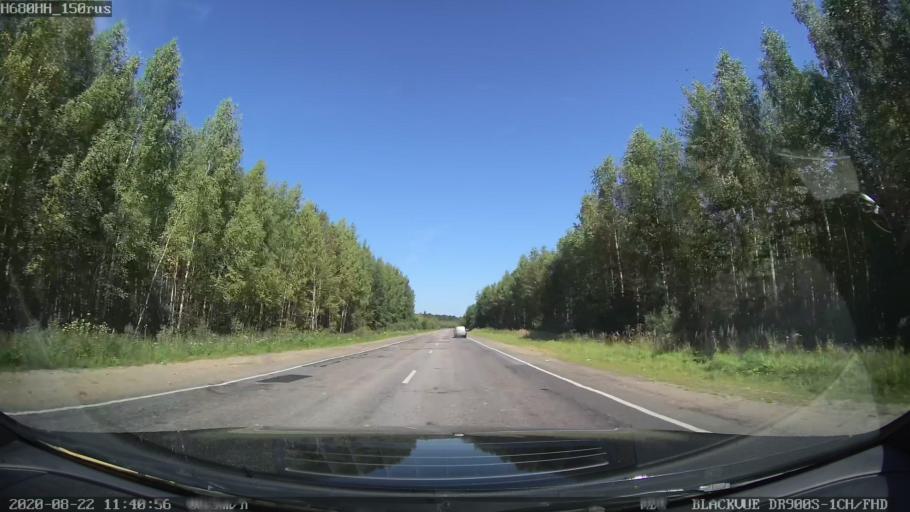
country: RU
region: Tverskaya
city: Sakharovo
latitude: 56.9832
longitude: 36.0237
